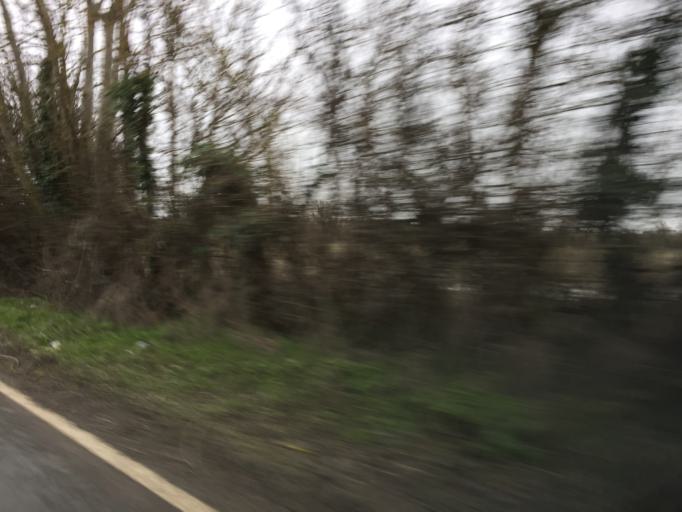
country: GB
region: England
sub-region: Oxfordshire
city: Wantage
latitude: 51.5951
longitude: -1.4622
